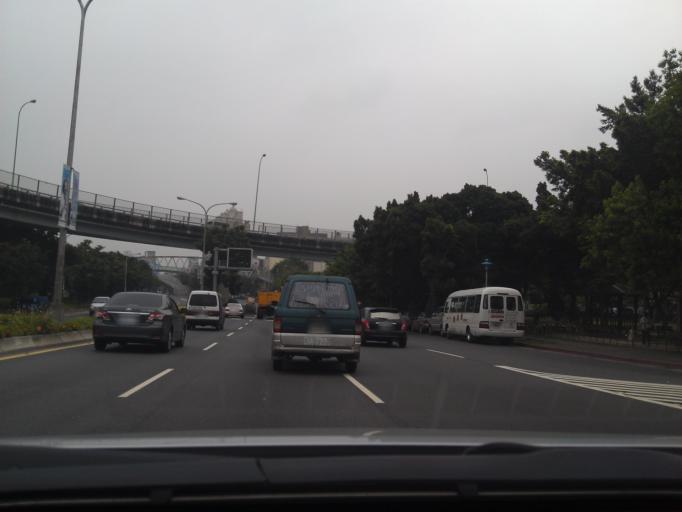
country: TW
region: Taipei
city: Taipei
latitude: 25.0814
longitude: 121.5078
